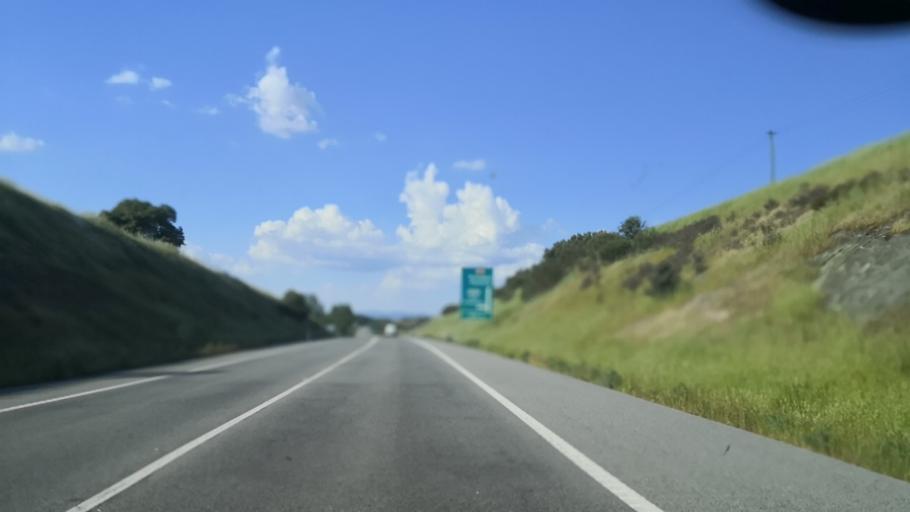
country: PT
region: Portalegre
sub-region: Arronches
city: Arronches
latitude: 39.0356
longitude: -7.4524
